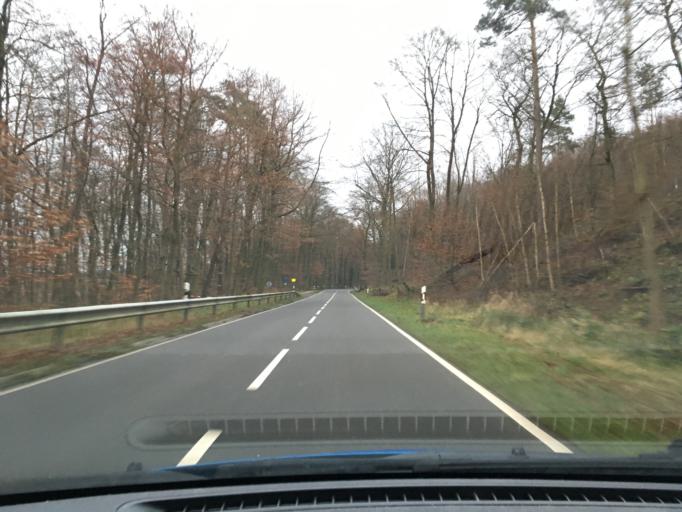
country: DE
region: Lower Saxony
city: Tosterglope
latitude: 53.2512
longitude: 10.8233
